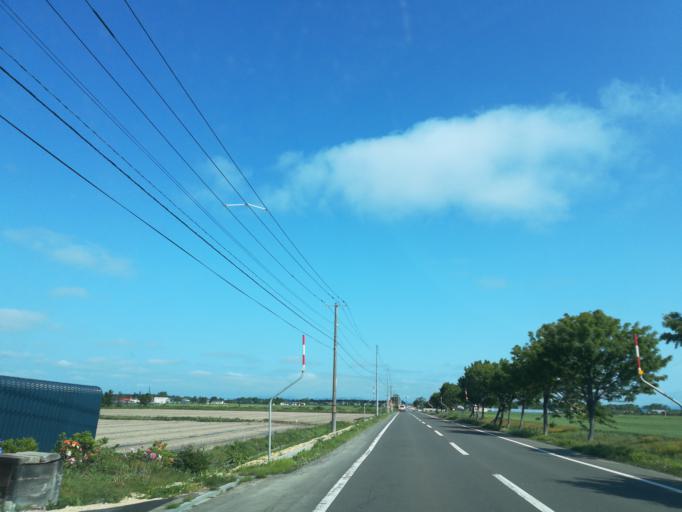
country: JP
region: Hokkaido
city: Iwamizawa
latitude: 43.1735
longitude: 141.7281
